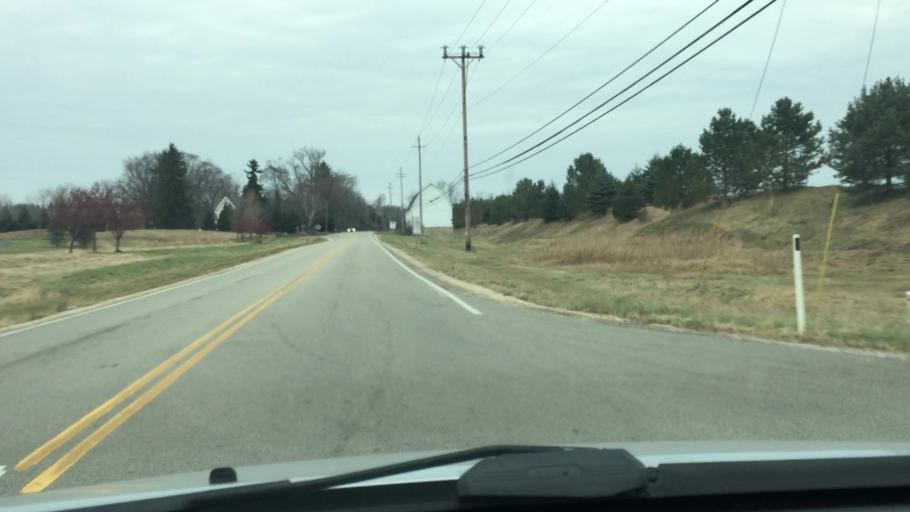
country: US
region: Wisconsin
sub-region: Ozaukee County
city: Thiensville
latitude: 43.2508
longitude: -87.9823
